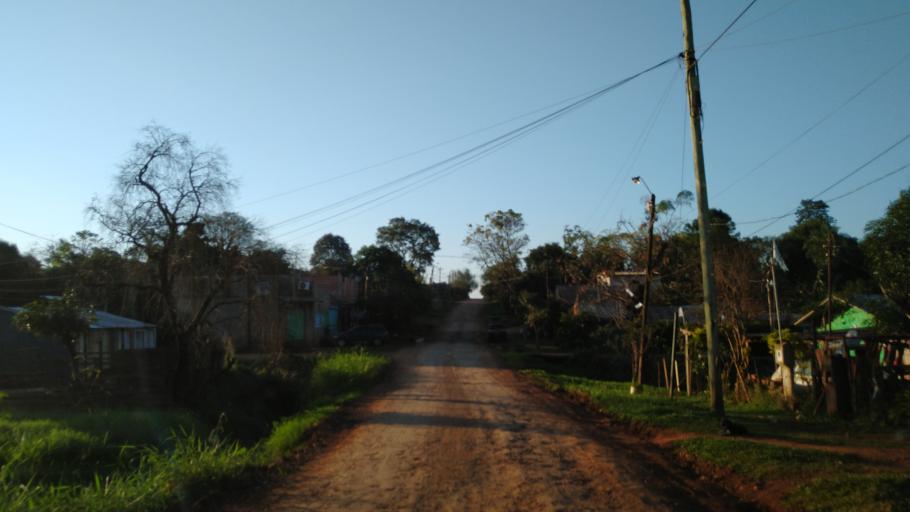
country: AR
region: Misiones
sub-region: Departamento de Capital
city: Posadas
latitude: -27.4213
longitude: -55.9204
